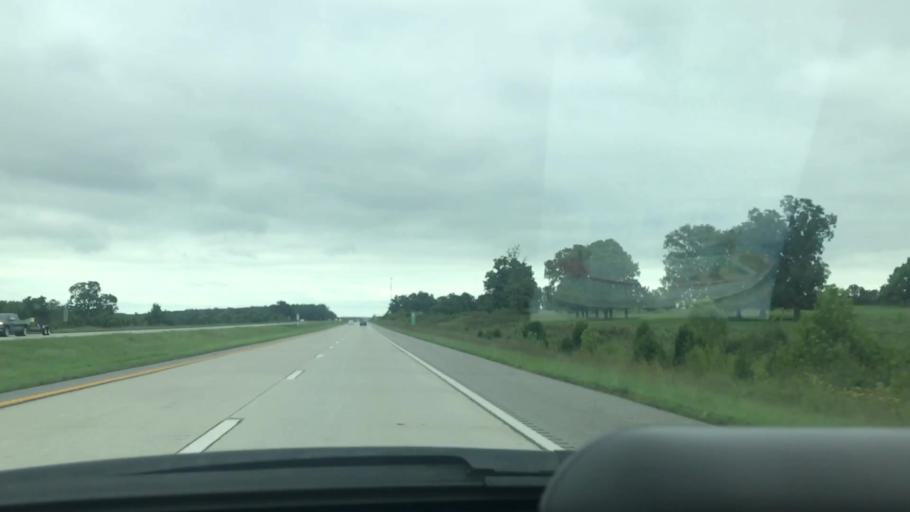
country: US
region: Missouri
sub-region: Greene County
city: Fair Grove
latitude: 37.4941
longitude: -93.1390
